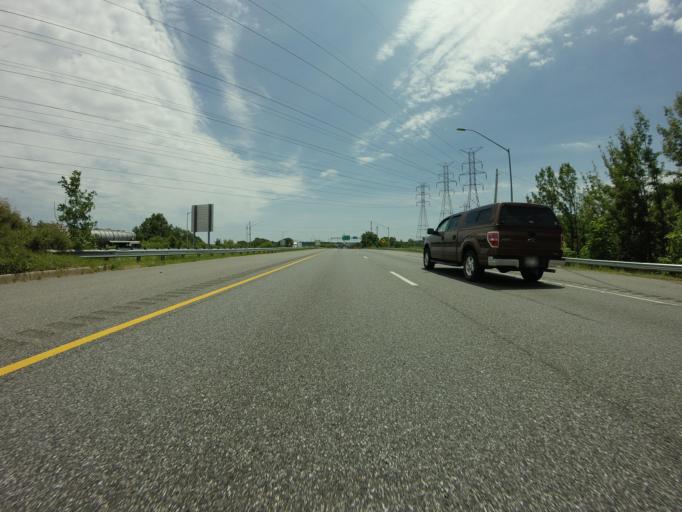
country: US
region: Maryland
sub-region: Baltimore County
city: Rosedale
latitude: 39.3100
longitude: -76.5023
